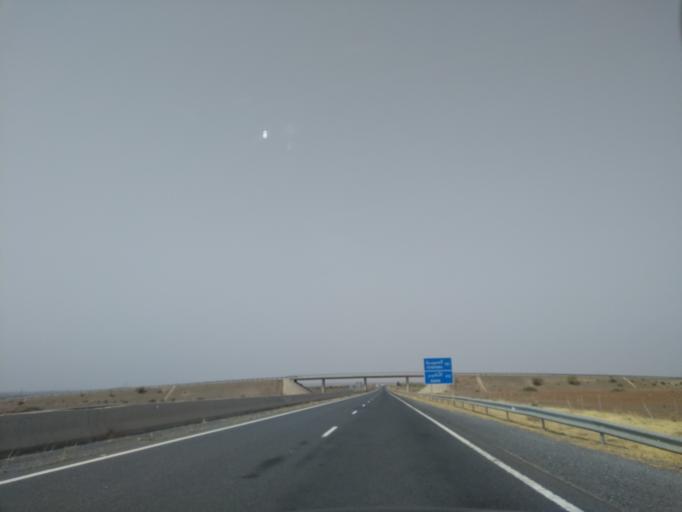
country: MA
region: Marrakech-Tensift-Al Haouz
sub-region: Marrakech
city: Marrakesh
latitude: 31.7668
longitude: -8.1763
